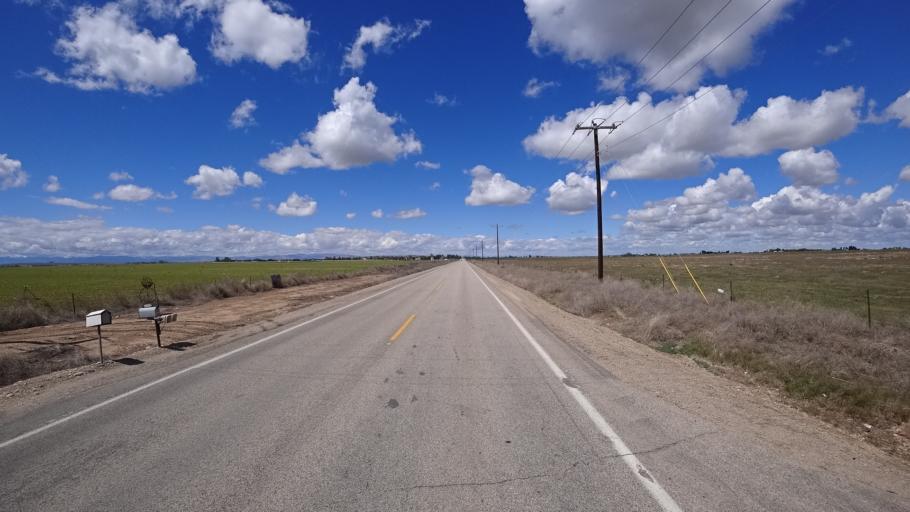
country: US
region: Idaho
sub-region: Ada County
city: Kuna
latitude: 43.4592
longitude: -116.3144
